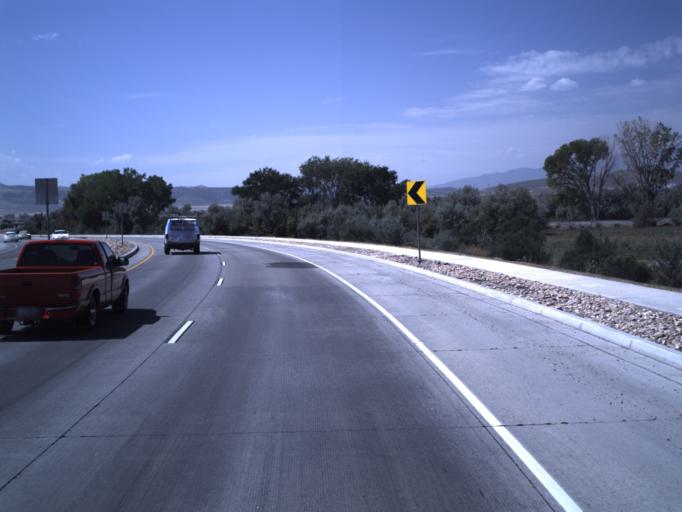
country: US
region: Utah
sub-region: Utah County
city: Saratoga Springs
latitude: 40.3760
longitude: -111.9022
